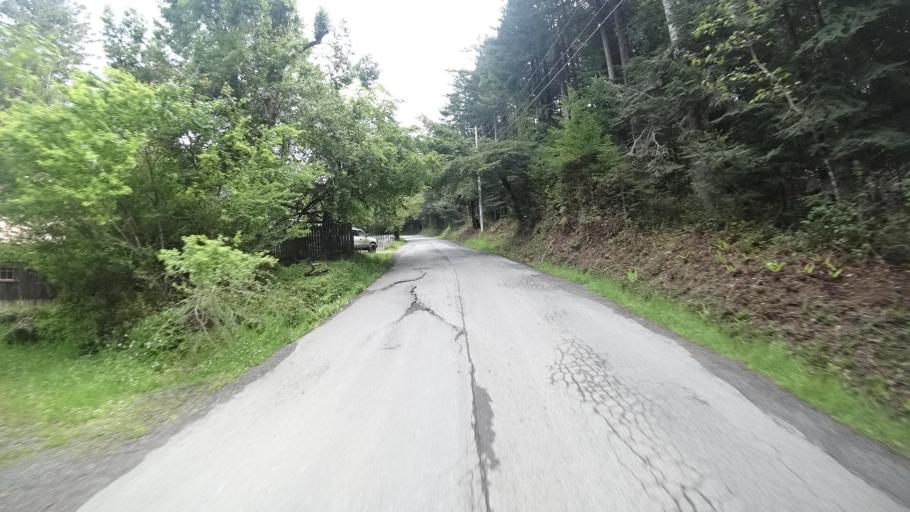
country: US
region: California
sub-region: Humboldt County
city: Blue Lake
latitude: 40.8988
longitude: -123.9937
